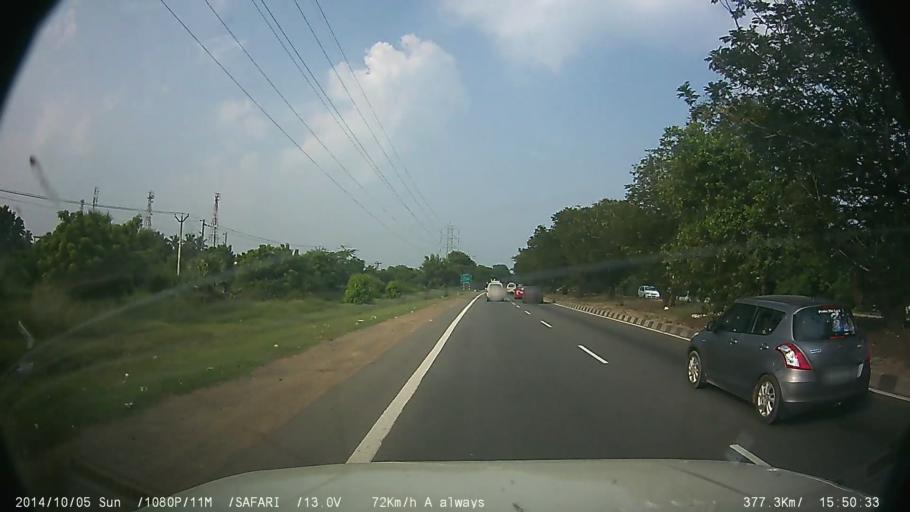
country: IN
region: Tamil Nadu
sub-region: Kancheepuram
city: Singapperumalkovil
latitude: 12.7830
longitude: 80.0130
